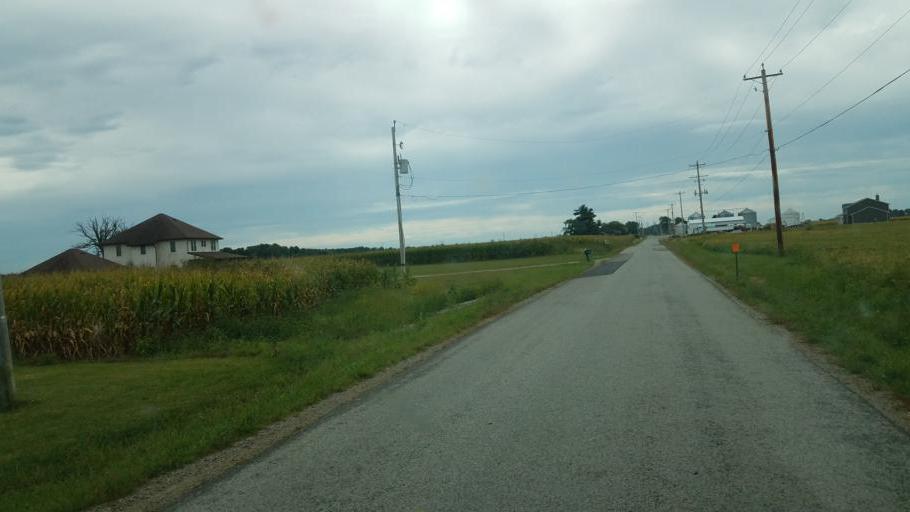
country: US
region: Ohio
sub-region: Knox County
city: Centerburg
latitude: 40.2825
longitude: -82.7225
